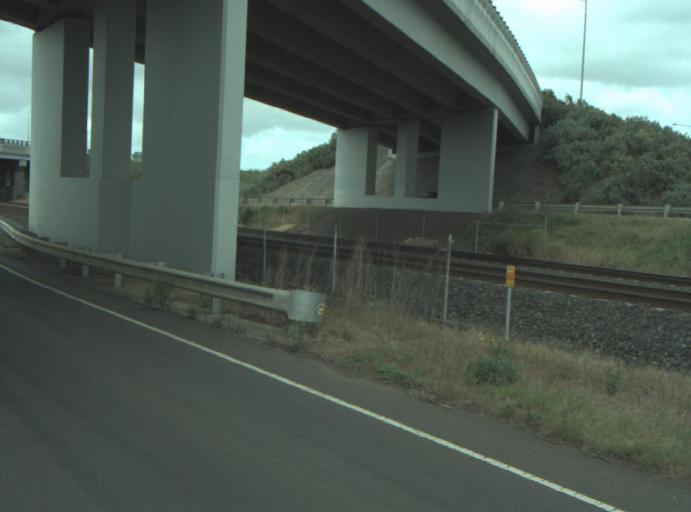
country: AU
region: Victoria
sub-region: Greater Geelong
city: Lara
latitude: -38.0555
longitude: 144.3903
